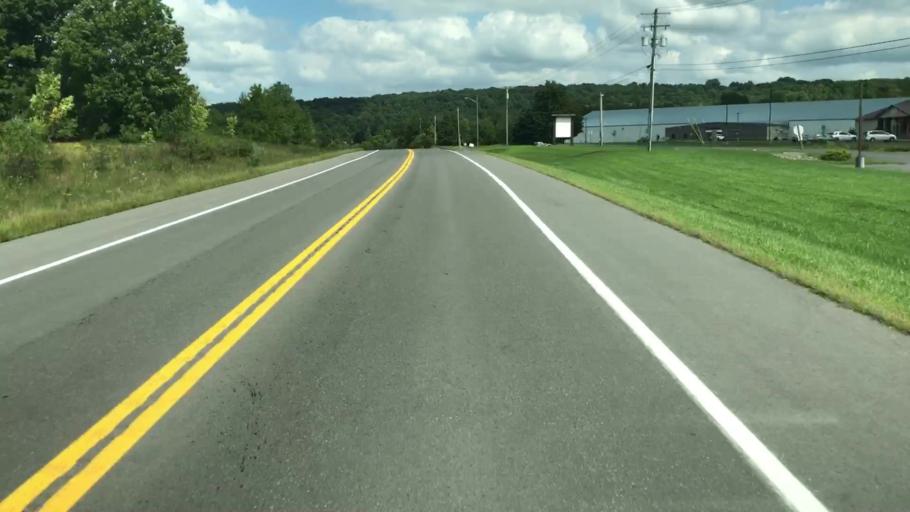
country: US
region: New York
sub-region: Onondaga County
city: Marcellus
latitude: 42.9538
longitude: -76.3461
